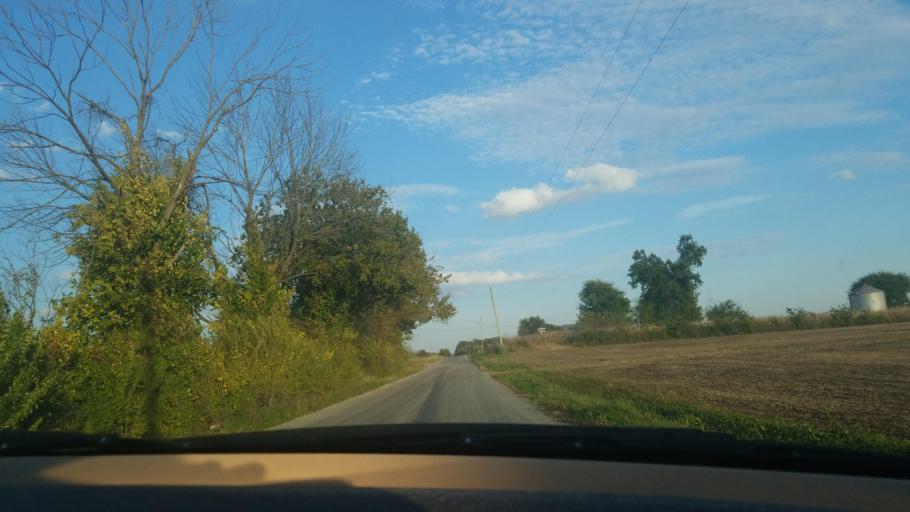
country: US
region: Illinois
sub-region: Saline County
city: Carrier Mills
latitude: 37.8050
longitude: -88.6805
